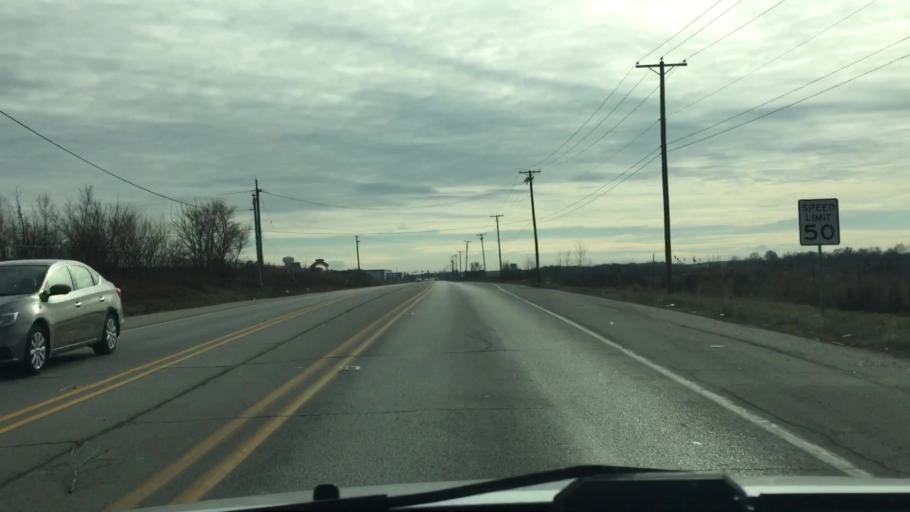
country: US
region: Illinois
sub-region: Kane County
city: South Elgin
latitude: 42.0065
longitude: -88.2690
